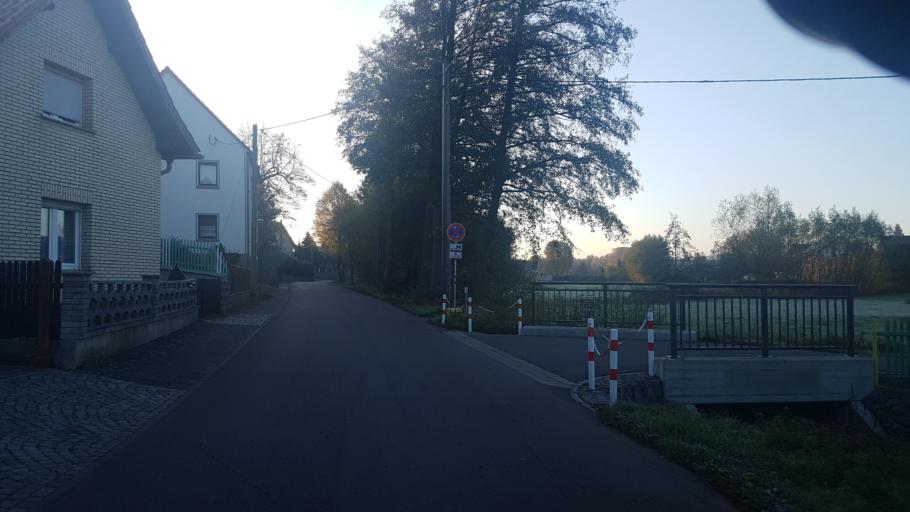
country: DE
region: Saxony
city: Schildau
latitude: 51.4430
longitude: 12.9694
